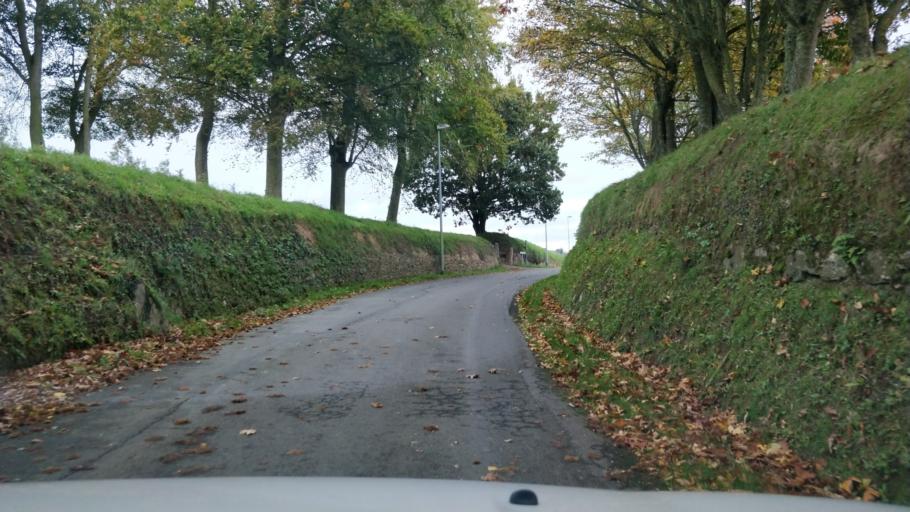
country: FR
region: Brittany
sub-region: Departement des Cotes-d'Armor
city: Minihy-Treguier
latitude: 48.7742
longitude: -3.2312
